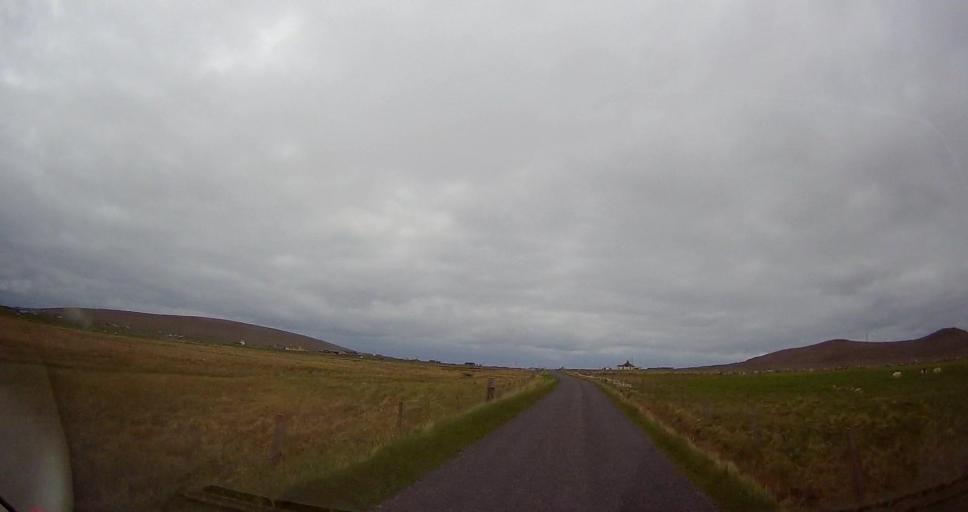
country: GB
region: Scotland
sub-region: Shetland Islands
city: Shetland
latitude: 60.7937
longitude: -0.8524
